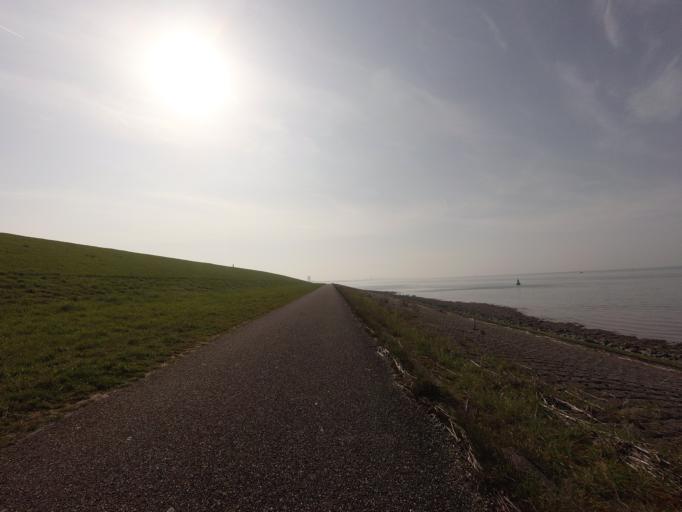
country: NL
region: Zeeland
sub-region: Gemeente Terneuzen
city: Zaamslag
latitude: 51.3464
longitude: 3.8782
